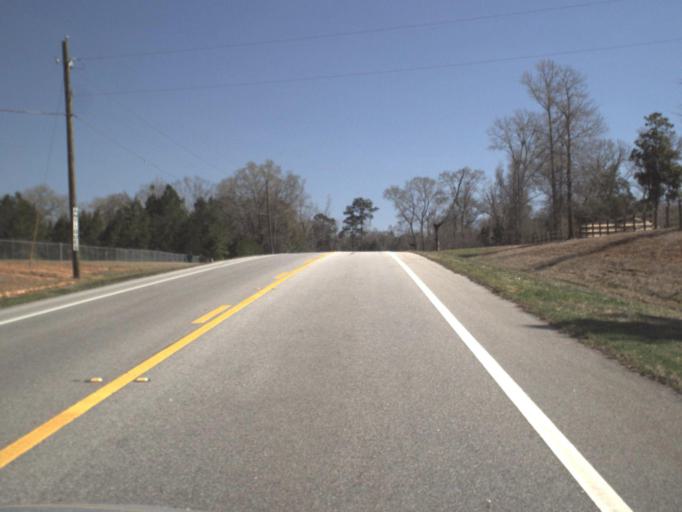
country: US
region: Florida
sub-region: Jackson County
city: Marianna
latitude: 30.8048
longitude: -85.2833
